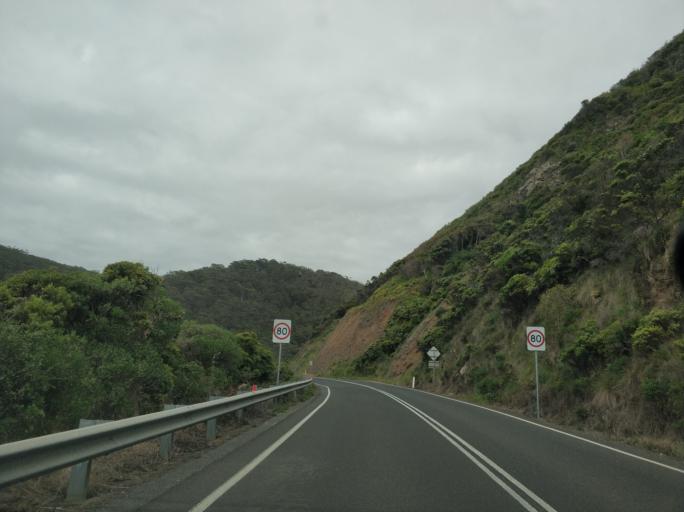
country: AU
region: Victoria
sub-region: Surf Coast
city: Anglesea
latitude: -38.5550
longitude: 143.9809
